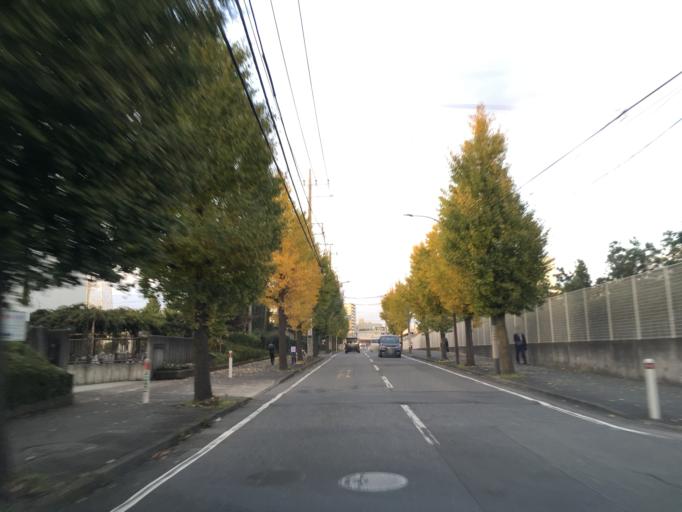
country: JP
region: Tokyo
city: Hachioji
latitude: 35.5891
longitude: 139.3461
